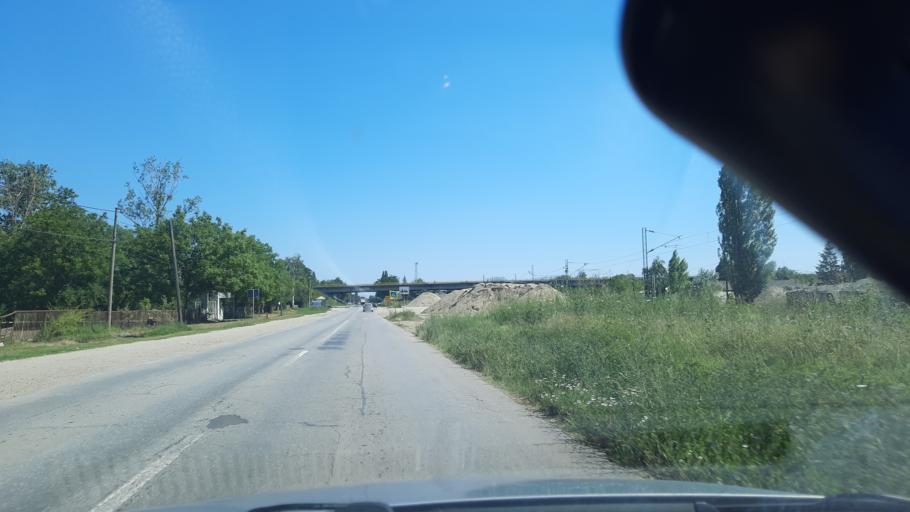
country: RS
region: Central Serbia
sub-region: Podunavski Okrug
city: Smederevo
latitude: 44.5904
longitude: 20.9974
